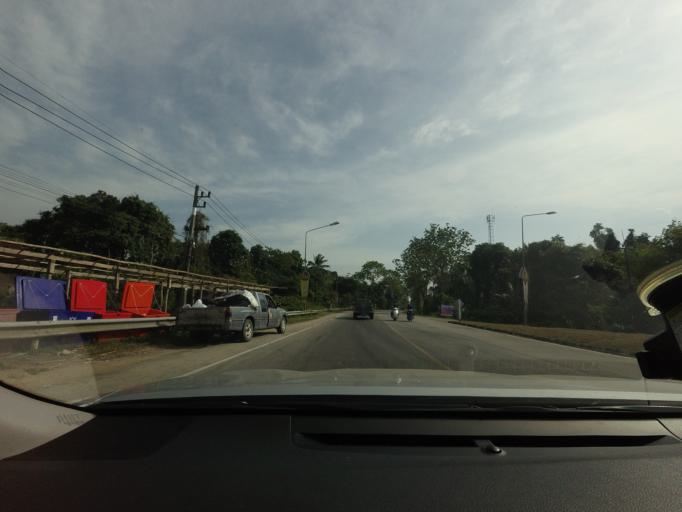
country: TH
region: Narathiwat
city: Ra-ngae
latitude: 6.3249
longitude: 101.7887
